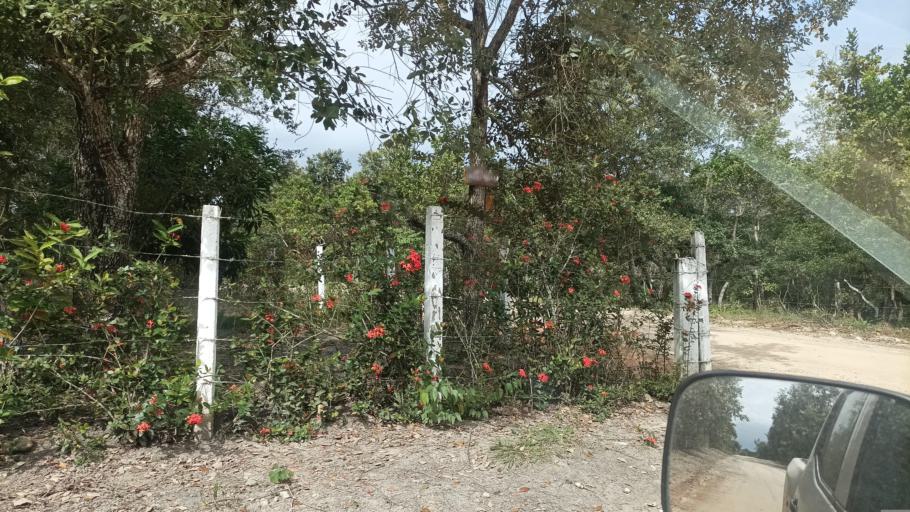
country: MX
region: Veracruz
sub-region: Cosoleacaque
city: Coacotla
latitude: 17.9467
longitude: -94.7097
